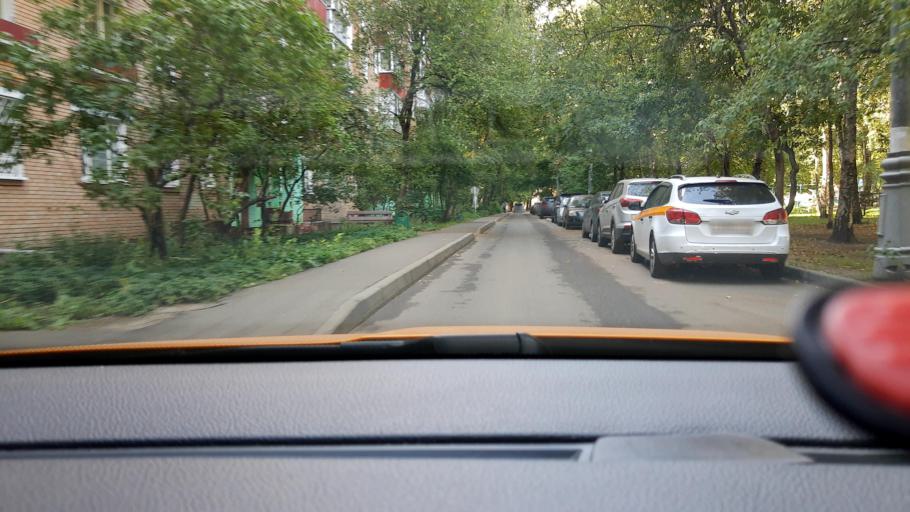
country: RU
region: Moscow
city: Ivanovskoye
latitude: 55.7546
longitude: 37.8365
